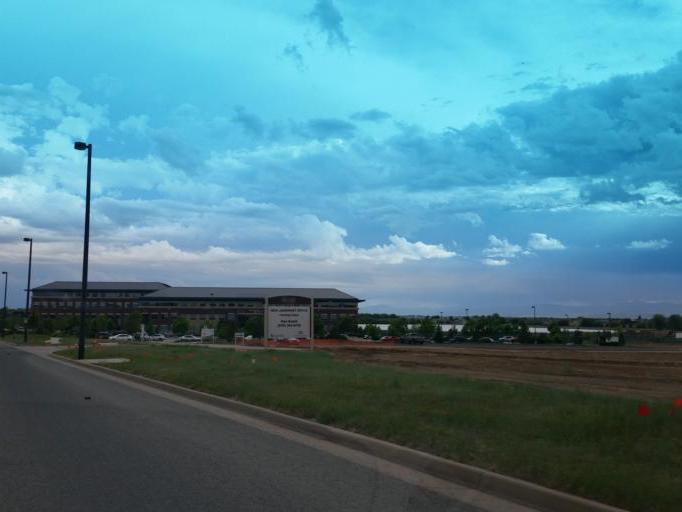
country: US
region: Colorado
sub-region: Larimer County
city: Loveland
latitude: 40.4242
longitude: -105.0022
